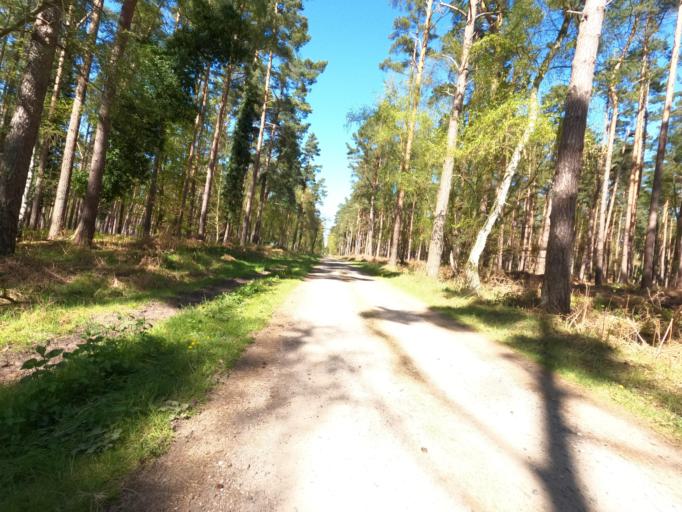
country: DE
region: Mecklenburg-Vorpommern
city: Born
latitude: 54.4088
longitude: 12.5301
